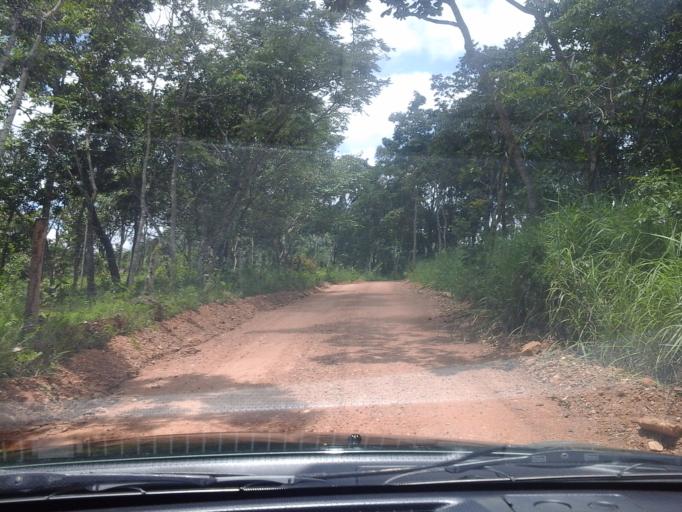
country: BR
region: Goias
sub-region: Pirenopolis
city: Pirenopolis
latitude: -15.7330
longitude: -49.0337
